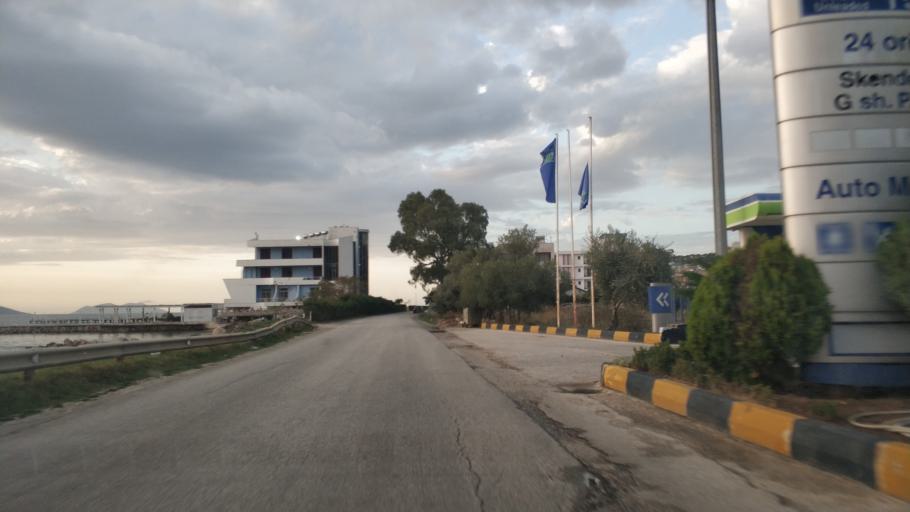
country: AL
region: Vlore
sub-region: Rrethi i Vlores
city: Orikum
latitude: 40.3544
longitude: 19.4843
